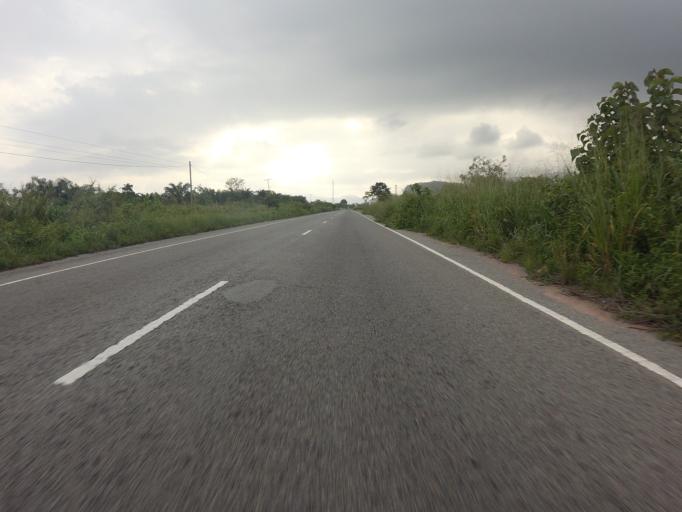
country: GH
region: Volta
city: Ho
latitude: 6.7806
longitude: 0.4666
